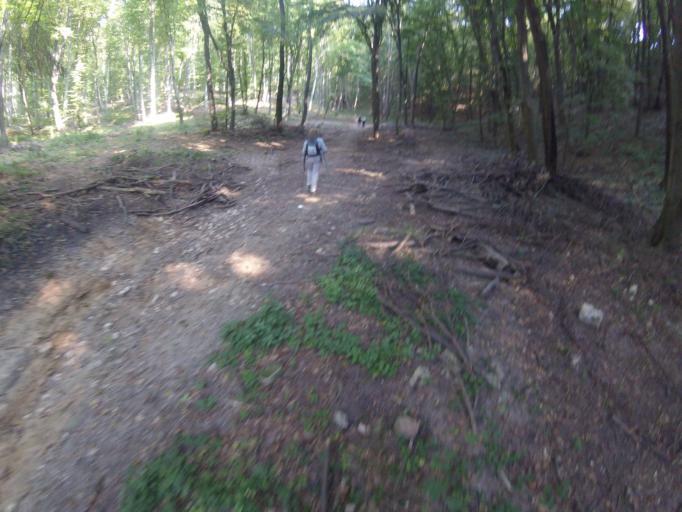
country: HU
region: Komarom-Esztergom
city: Piliscsev
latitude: 47.7099
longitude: 18.8393
